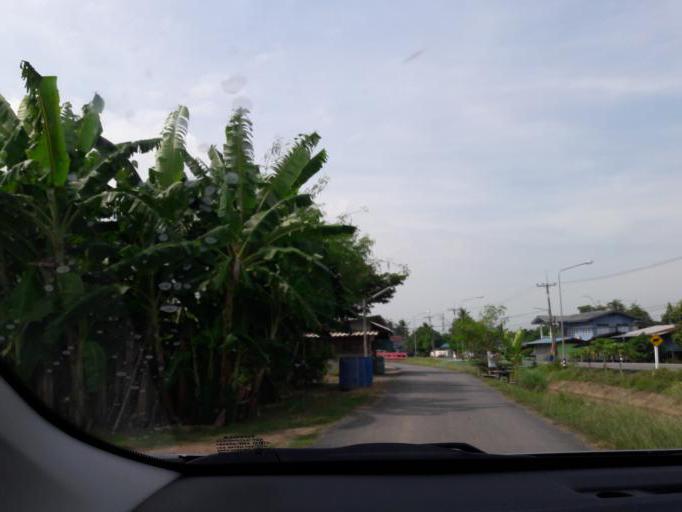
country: TH
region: Ang Thong
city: Ang Thong
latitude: 14.5738
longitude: 100.4687
